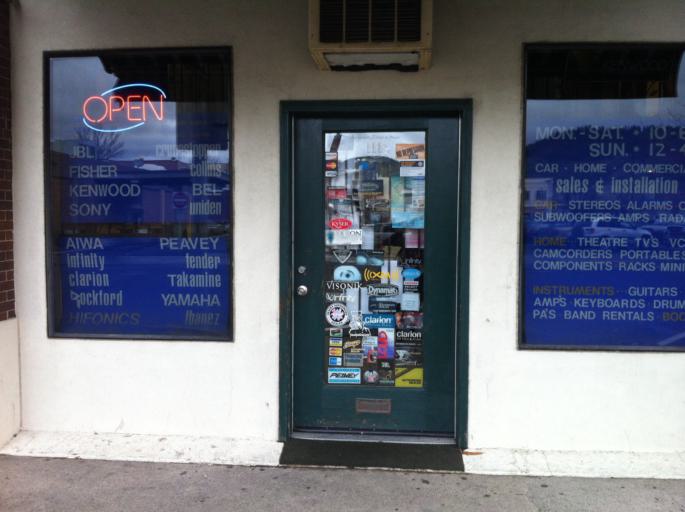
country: US
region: Oregon
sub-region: Union County
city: La Grande
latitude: 45.3270
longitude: -118.0928
